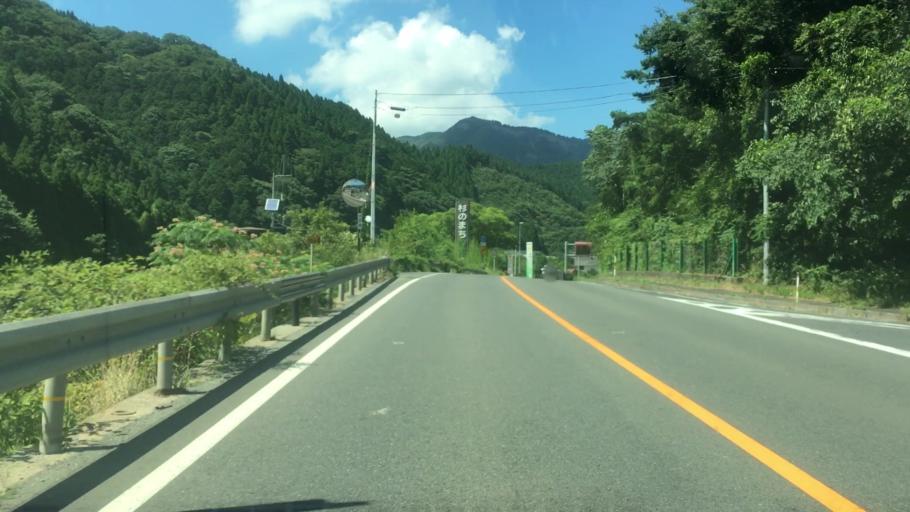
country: JP
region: Tottori
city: Tottori
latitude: 35.2739
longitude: 134.2240
